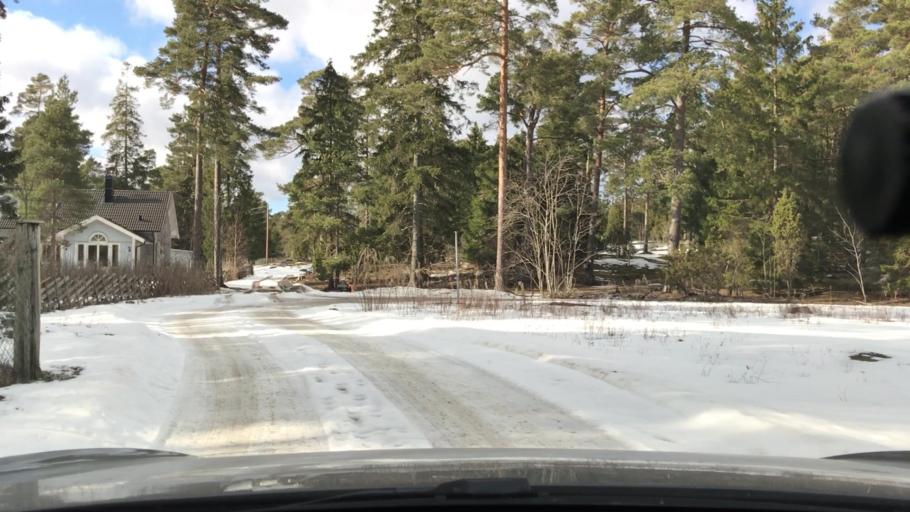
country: SE
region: Gotland
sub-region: Gotland
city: Slite
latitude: 57.3456
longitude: 18.7288
